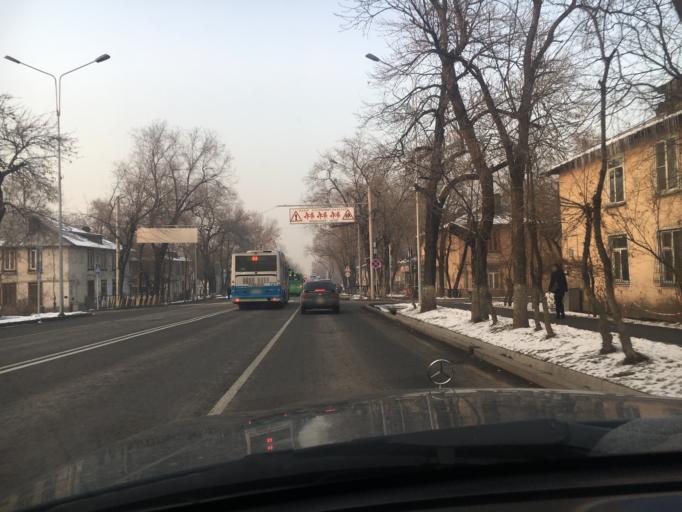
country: KZ
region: Almaty Qalasy
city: Almaty
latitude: 43.2081
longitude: 76.8791
